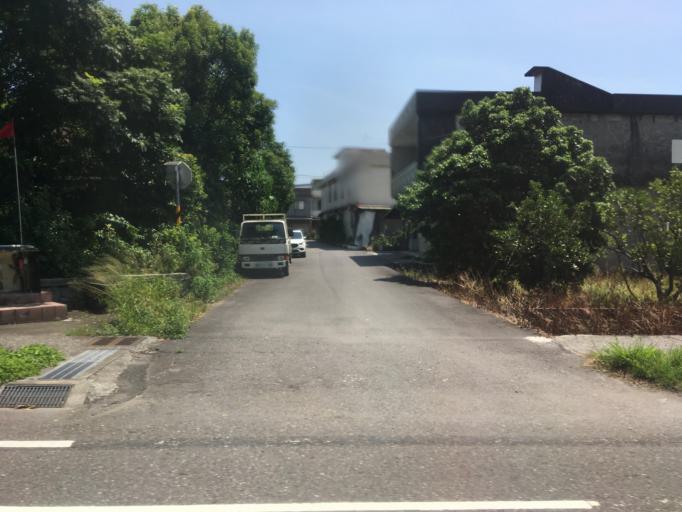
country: TW
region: Taiwan
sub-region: Yilan
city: Yilan
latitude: 24.6120
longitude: 121.8528
